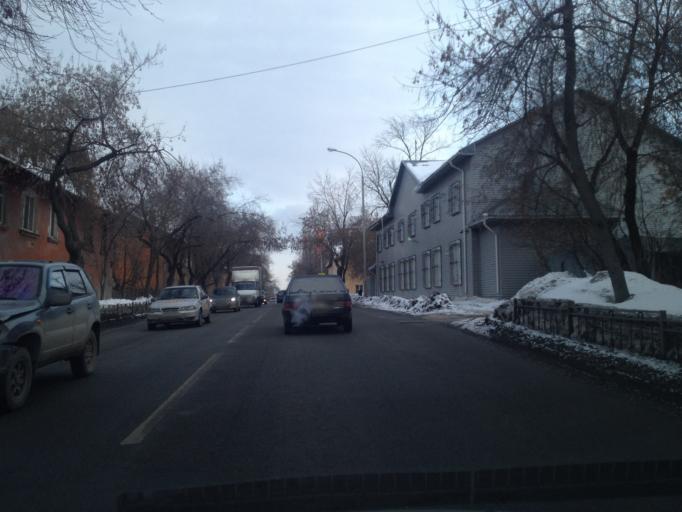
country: RU
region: Sverdlovsk
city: Yekaterinburg
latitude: 56.8648
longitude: 60.5724
